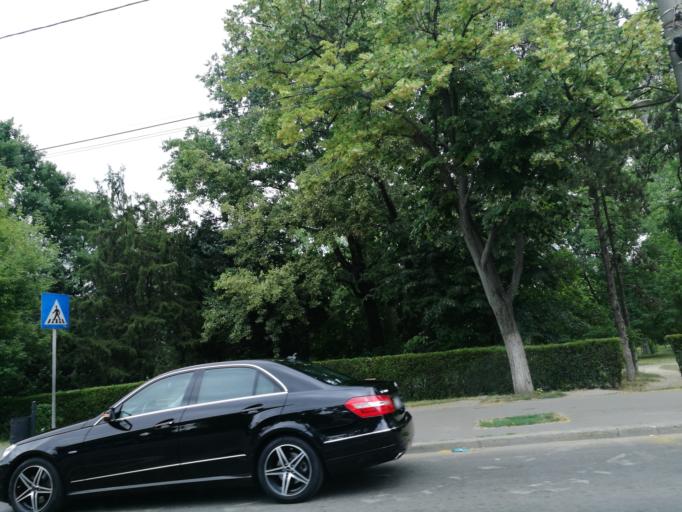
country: RO
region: Constanta
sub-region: Municipiul Constanta
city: Constanta
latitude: 44.2089
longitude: 28.6290
